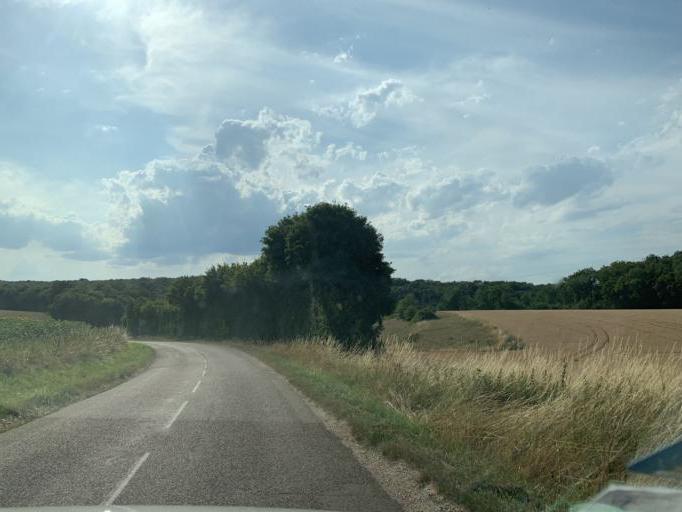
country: FR
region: Bourgogne
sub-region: Departement de l'Yonne
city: Fontenailles
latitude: 47.5189
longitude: 3.4142
